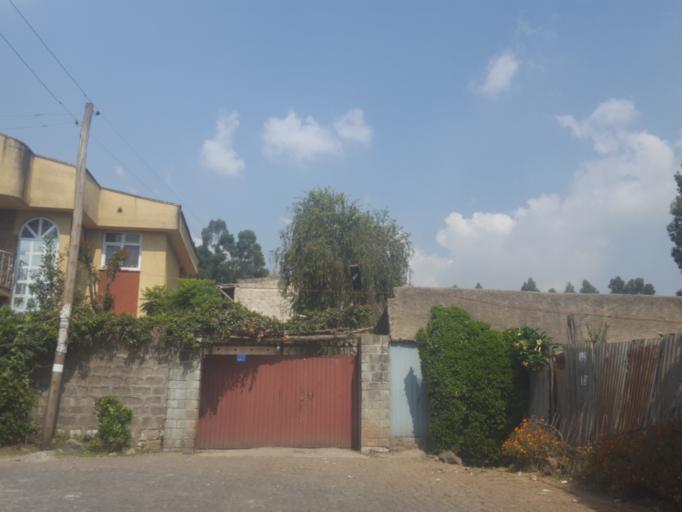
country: ET
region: Adis Abeba
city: Addis Ababa
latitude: 9.0648
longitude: 38.7214
